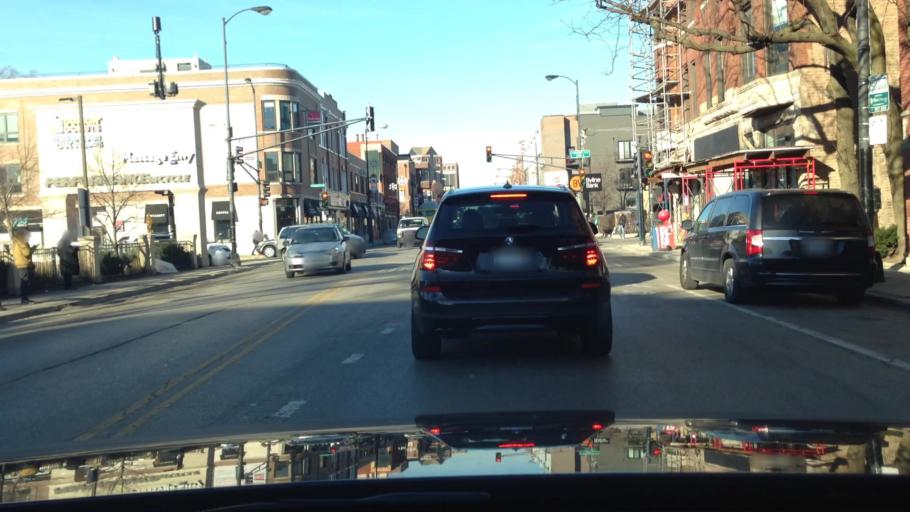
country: US
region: Illinois
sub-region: Cook County
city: Chicago
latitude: 41.9322
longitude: -87.6490
